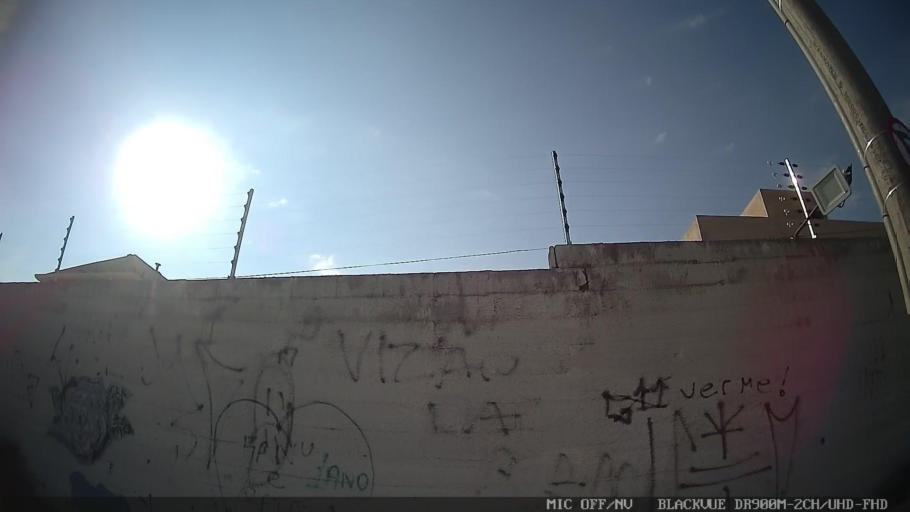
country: BR
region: Sao Paulo
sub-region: Indaiatuba
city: Indaiatuba
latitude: -23.0858
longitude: -47.2366
